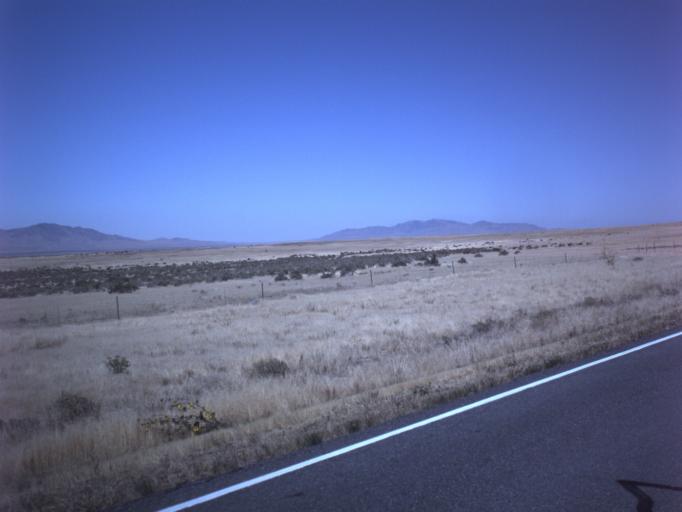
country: US
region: Utah
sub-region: Tooele County
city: Grantsville
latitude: 40.5712
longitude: -112.7302
